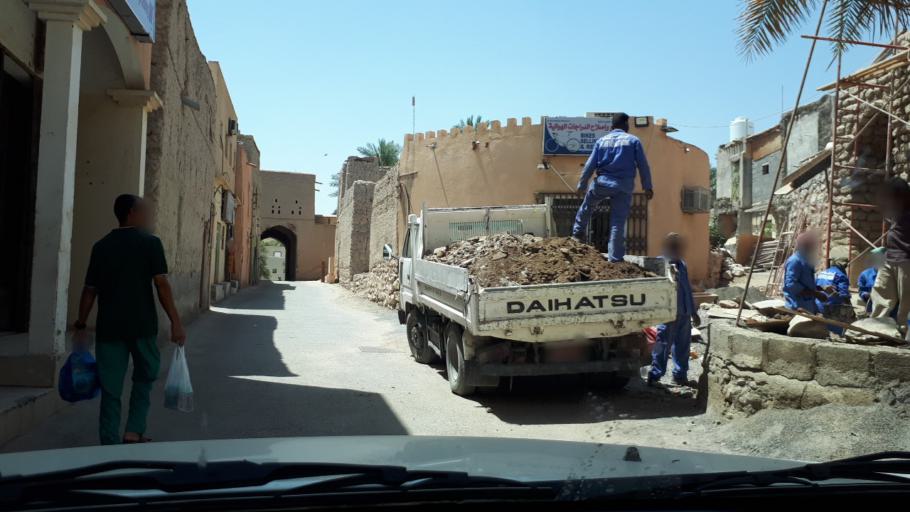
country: OM
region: Muhafazat ad Dakhiliyah
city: Nizwa
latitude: 22.9304
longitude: 57.5317
